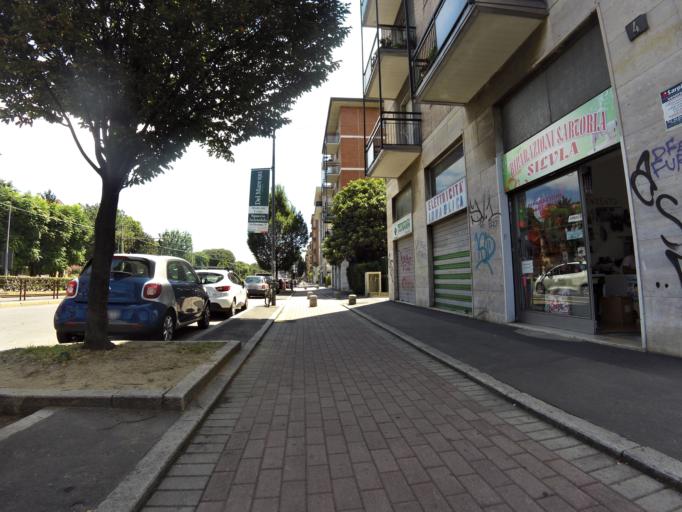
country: IT
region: Lombardy
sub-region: Citta metropolitana di Milano
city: Linate
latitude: 45.4568
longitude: 9.2424
